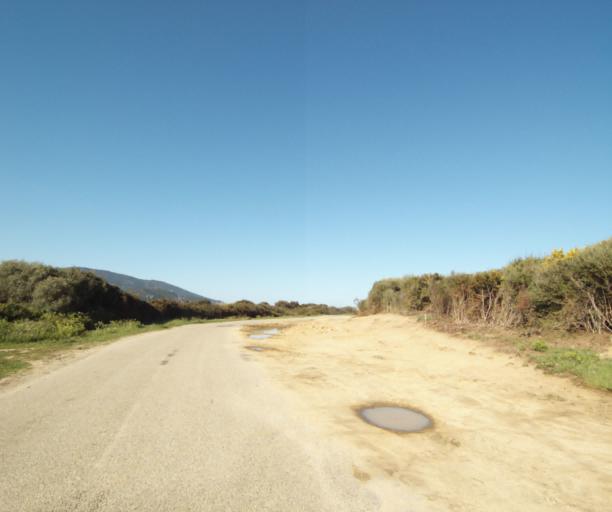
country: FR
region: Corsica
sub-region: Departement de la Corse-du-Sud
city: Propriano
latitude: 41.6637
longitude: 8.8859
